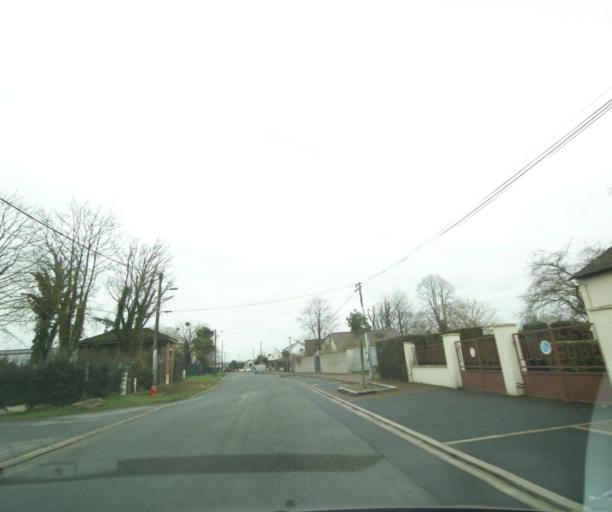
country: FR
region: Picardie
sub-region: Departement de l'Oise
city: Noyon
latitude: 49.5740
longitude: 3.0156
